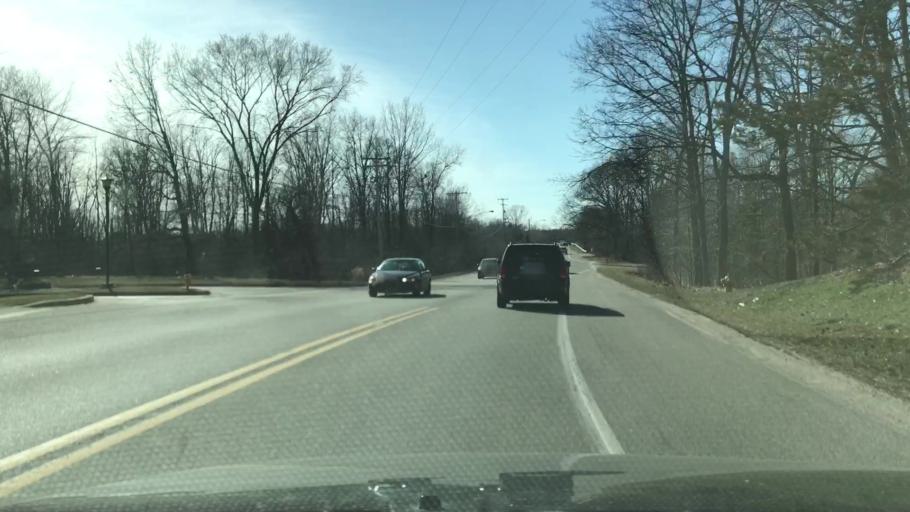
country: US
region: Michigan
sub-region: Kent County
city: Forest Hills
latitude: 42.9200
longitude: -85.5419
